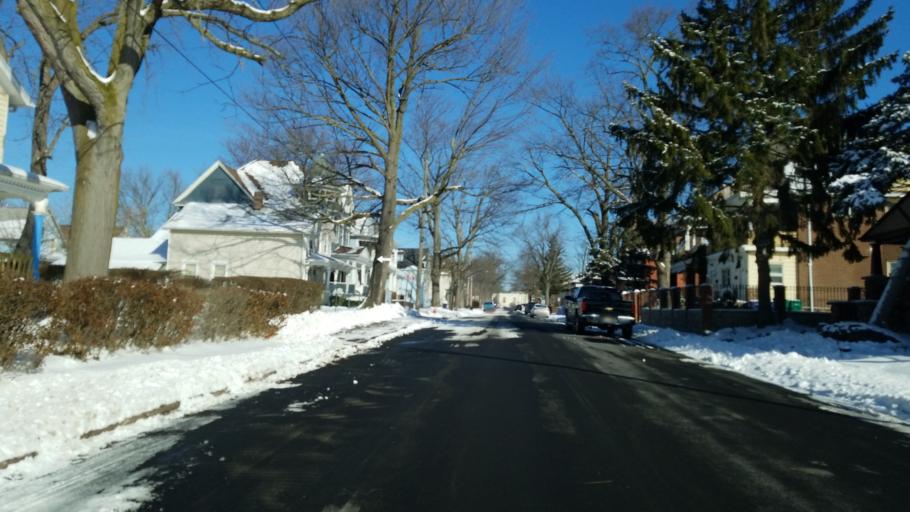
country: US
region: New York
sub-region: Niagara County
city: Niagara Falls
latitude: 43.0893
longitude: -79.0567
